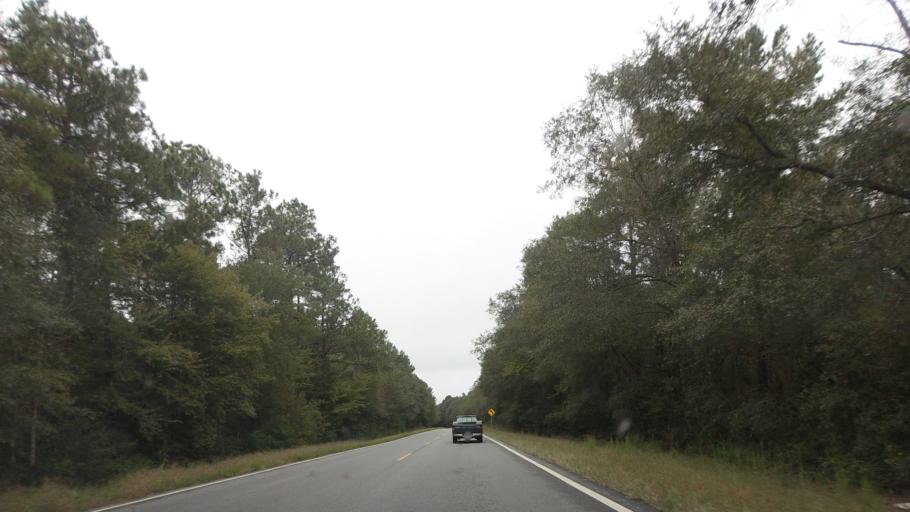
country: US
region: Georgia
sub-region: Berrien County
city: Enigma
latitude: 31.4166
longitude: -83.2433
